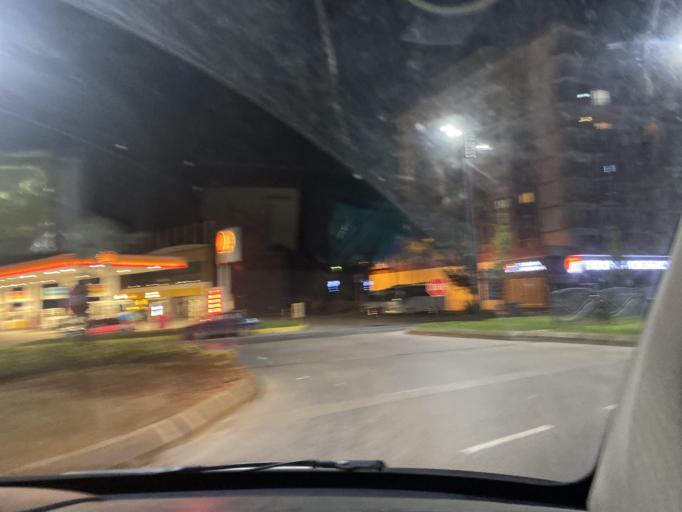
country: TR
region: Trabzon
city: Yomra
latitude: 40.9578
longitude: 39.8524
